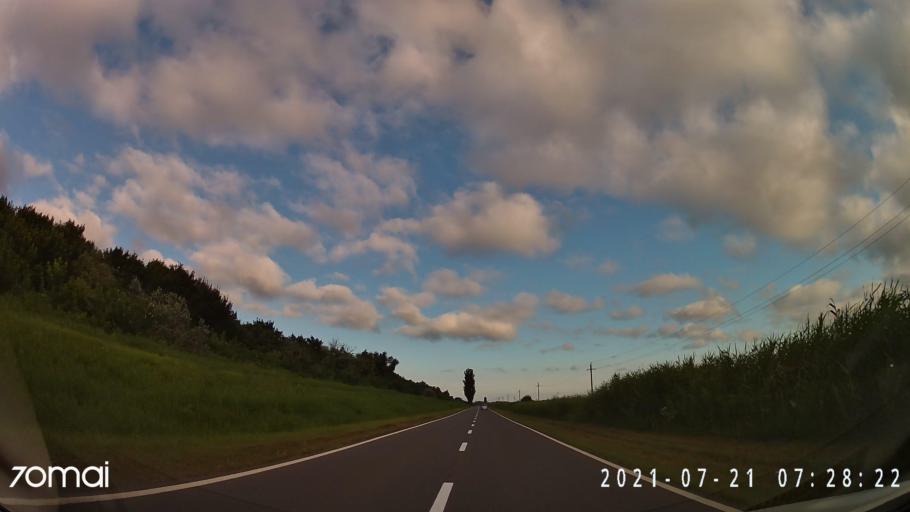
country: RO
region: Tulcea
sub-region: Comuna Luncavita
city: Rachelu
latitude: 45.3105
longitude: 28.3940
